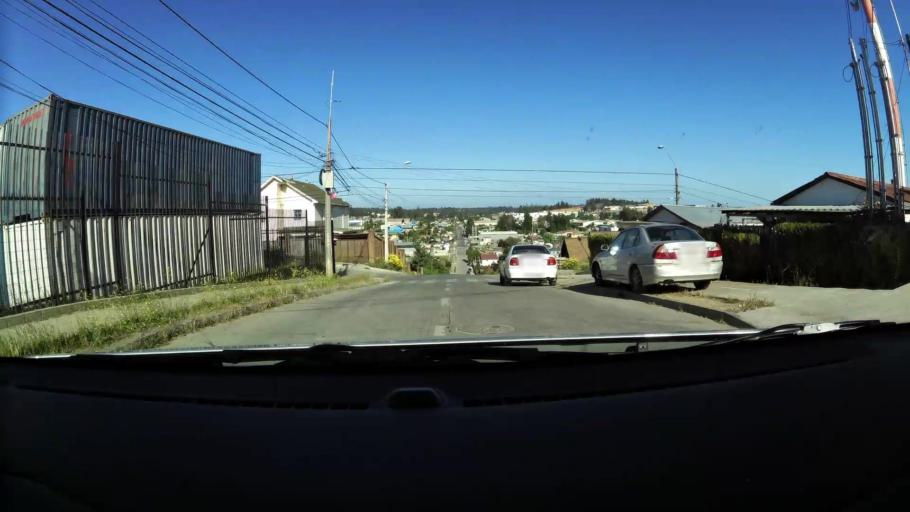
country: CL
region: Valparaiso
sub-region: Provincia de Valparaiso
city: Vina del Mar
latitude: -33.1151
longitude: -71.5711
